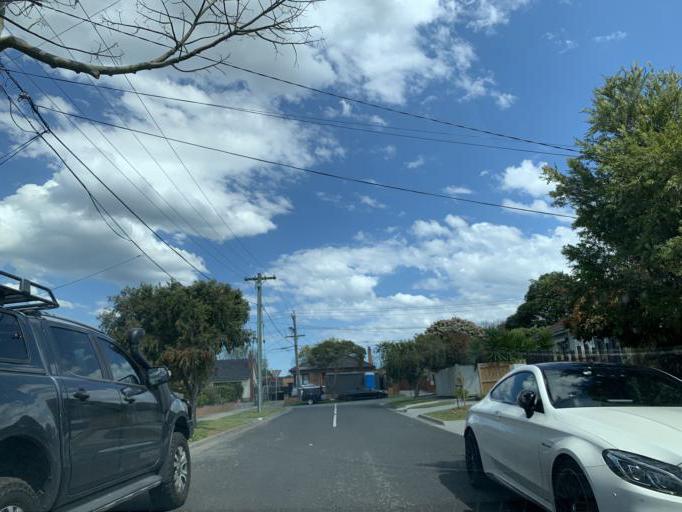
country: AU
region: Victoria
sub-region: Bayside
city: Moorabbin
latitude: -37.9405
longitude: 145.0437
